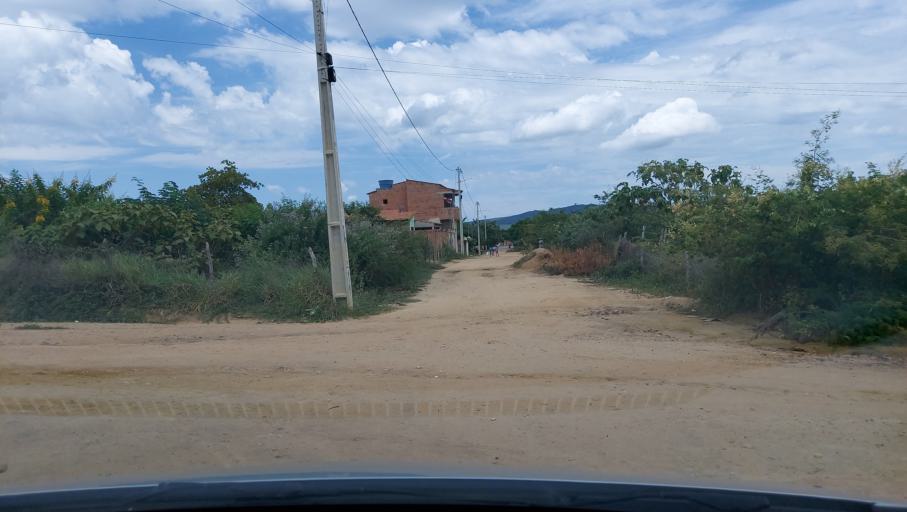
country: BR
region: Bahia
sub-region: Oliveira Dos Brejinhos
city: Beira Rio
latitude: -12.0071
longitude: -42.6313
